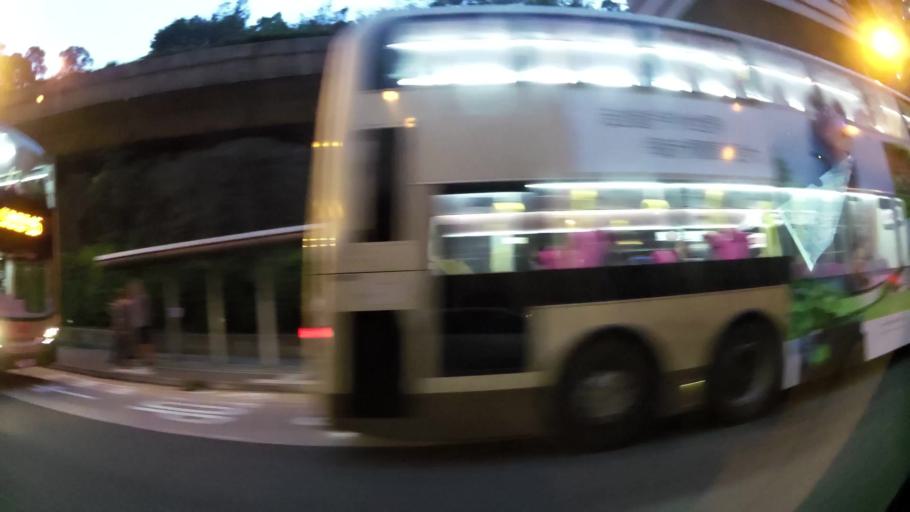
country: HK
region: Kowloon City
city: Kowloon
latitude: 22.3055
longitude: 114.2343
